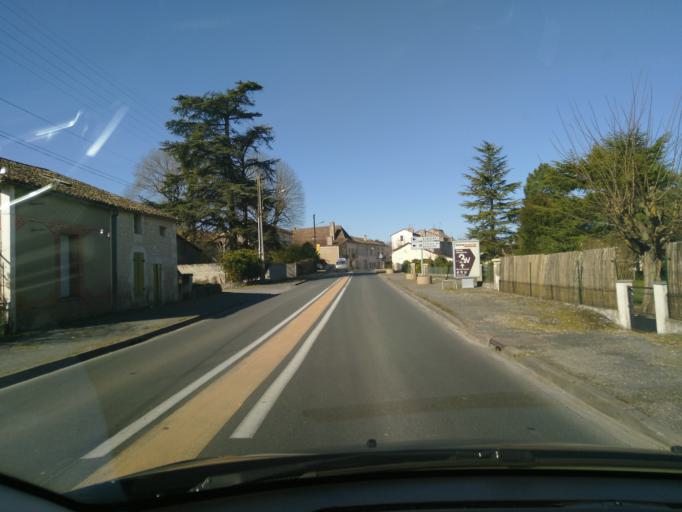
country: FR
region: Aquitaine
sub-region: Departement de la Dordogne
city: Monbazillac
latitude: 44.7573
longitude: 0.5275
